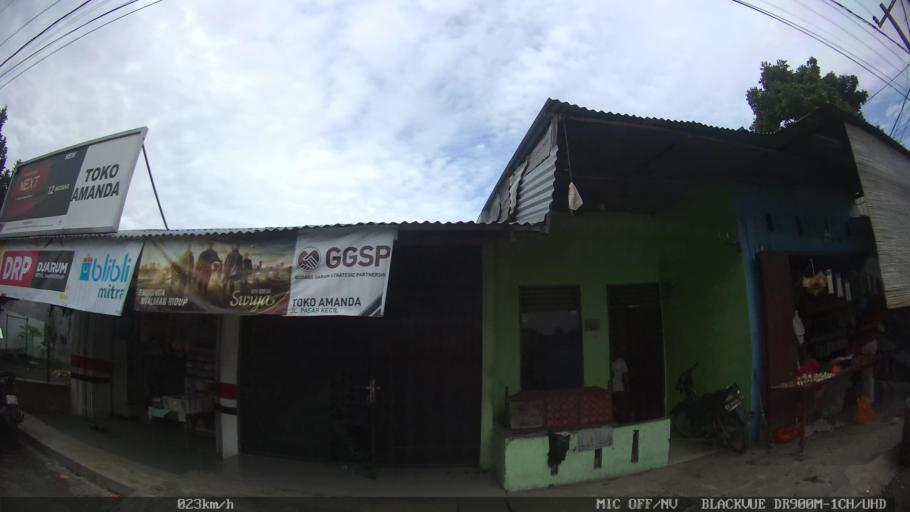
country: ID
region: North Sumatra
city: Sunggal
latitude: 3.5959
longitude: 98.5660
